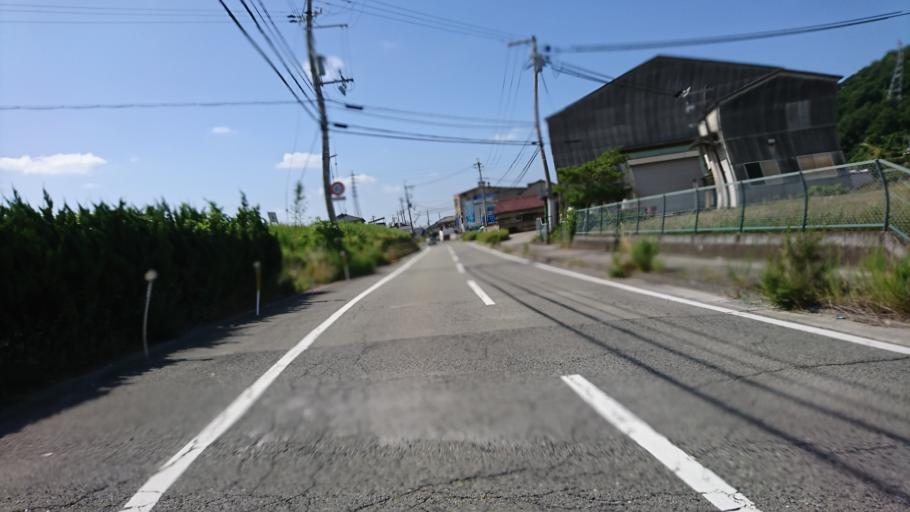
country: JP
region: Hyogo
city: Shirahamacho-usazakiminami
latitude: 34.7925
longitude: 134.7494
